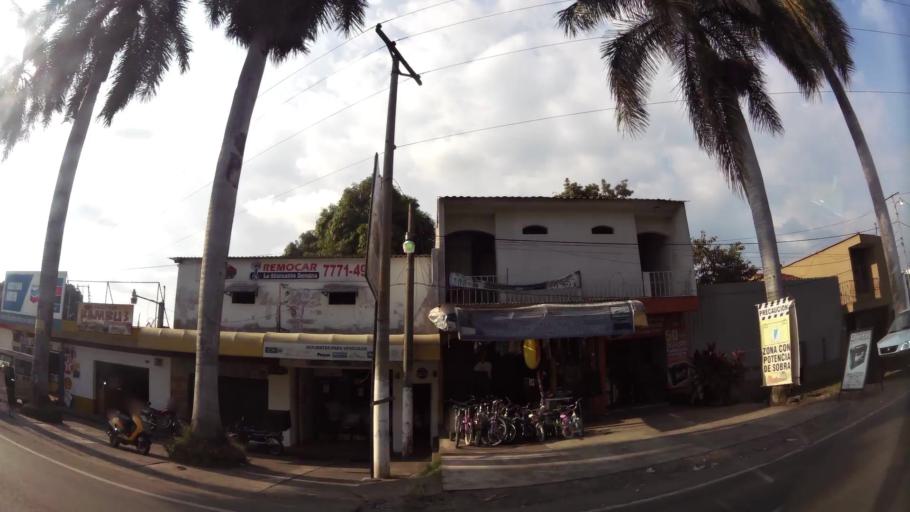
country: GT
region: Retalhuleu
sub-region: Municipio de Retalhuleu
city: Retalhuleu
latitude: 14.5335
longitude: -91.6743
